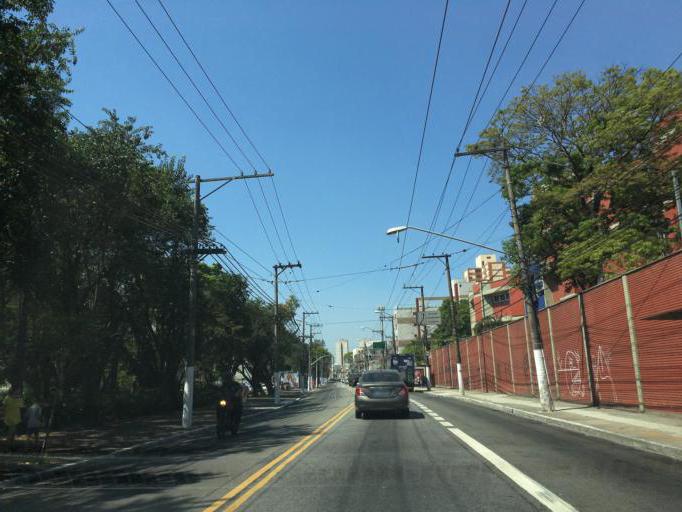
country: BR
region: Sao Paulo
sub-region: Sao Paulo
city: Sao Paulo
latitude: -23.5369
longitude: -46.5906
